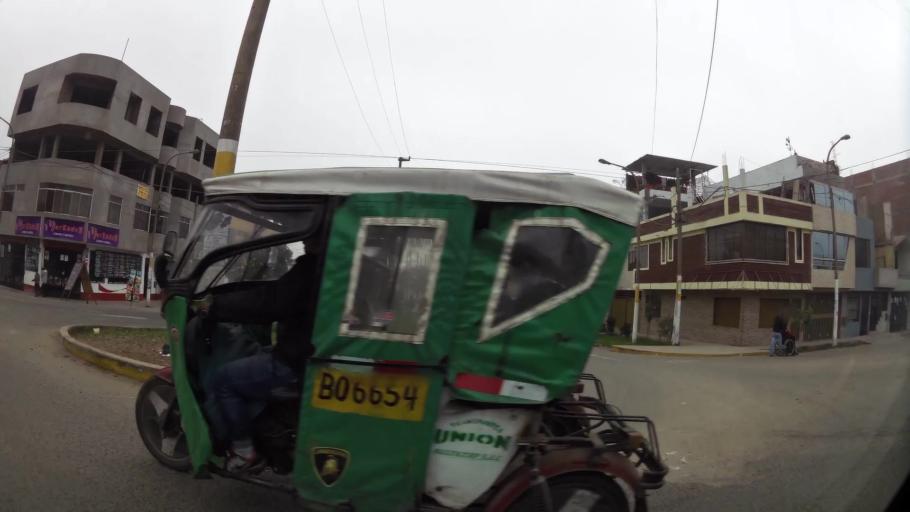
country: PE
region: Lima
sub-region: Lima
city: Urb. Santo Domingo
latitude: -11.8825
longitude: -77.0746
